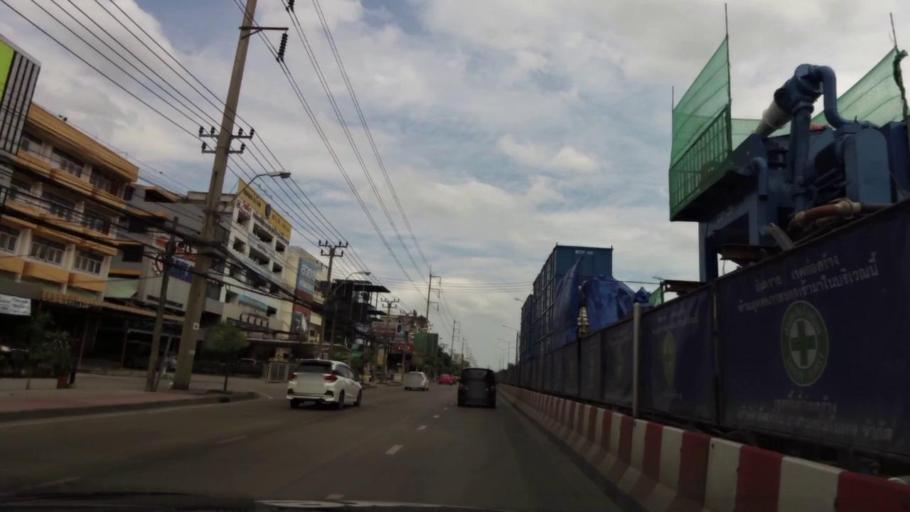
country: TH
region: Bangkok
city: Suan Luang
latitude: 13.7104
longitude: 100.6444
